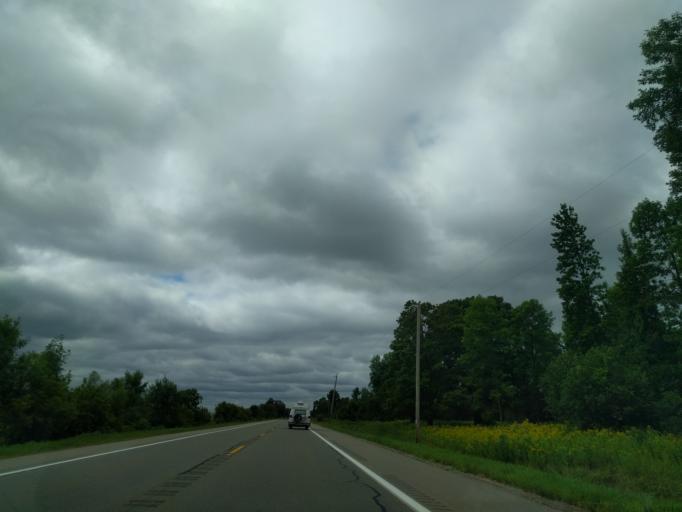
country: US
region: Michigan
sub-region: Menominee County
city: Menominee
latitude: 45.2521
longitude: -87.4863
